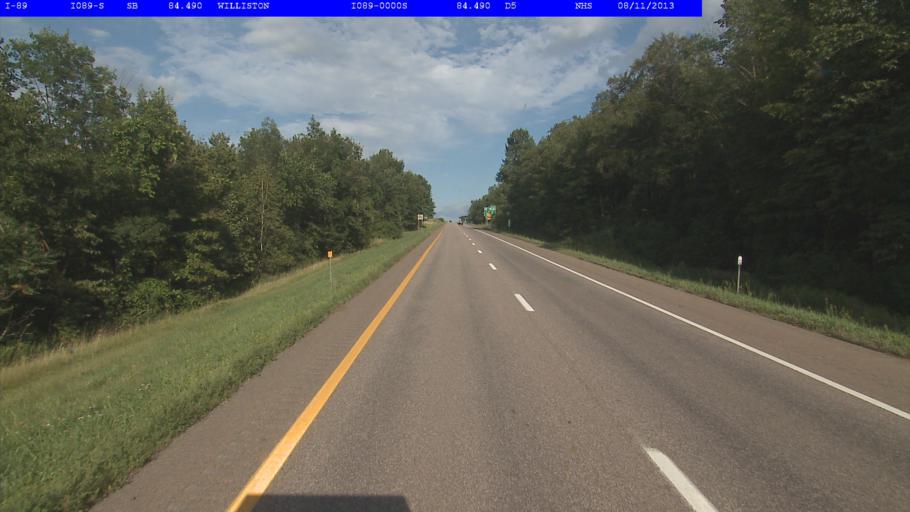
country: US
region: Vermont
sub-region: Chittenden County
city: Essex Junction
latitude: 44.4401
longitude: -73.1257
